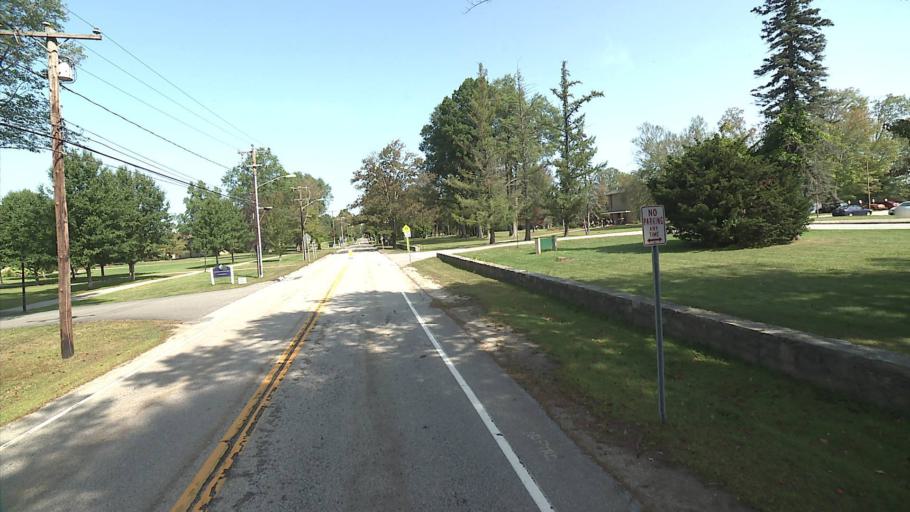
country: US
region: Connecticut
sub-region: Windham County
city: South Woodstock
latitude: 41.9274
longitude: -71.9567
